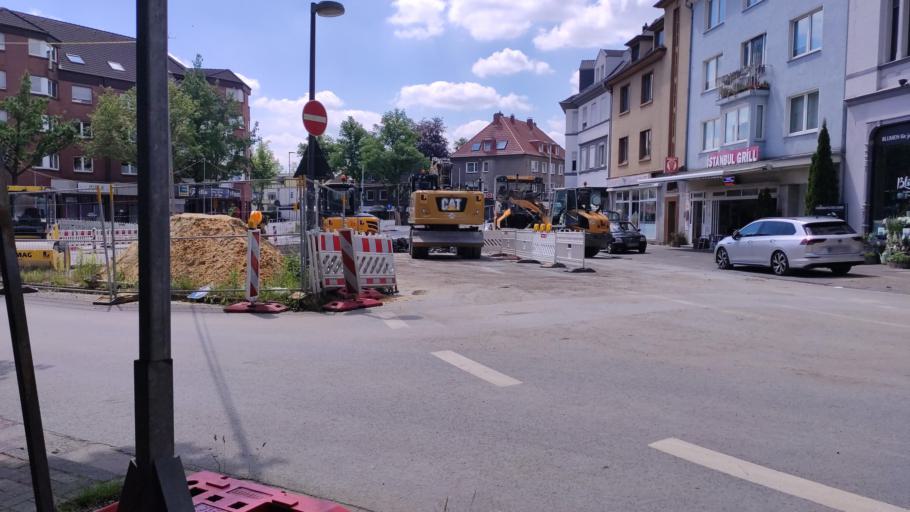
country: DE
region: North Rhine-Westphalia
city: Oer-Erkenschwick
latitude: 51.6094
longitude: 7.2612
